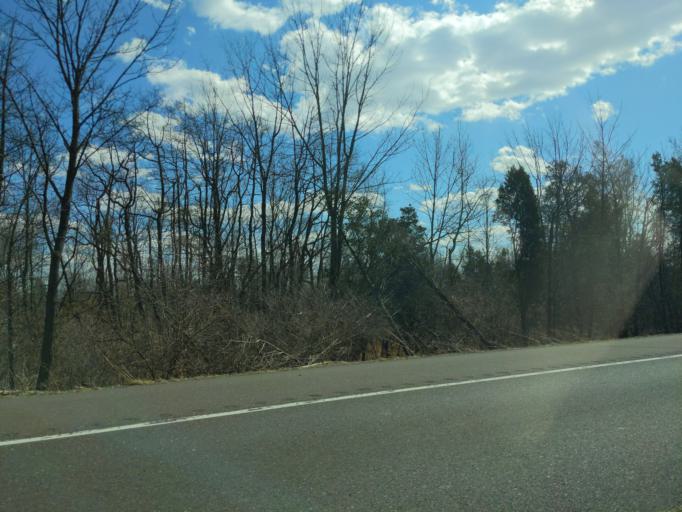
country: US
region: Pennsylvania
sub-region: Bucks County
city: Spinnerstown
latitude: 40.4169
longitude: -75.4561
